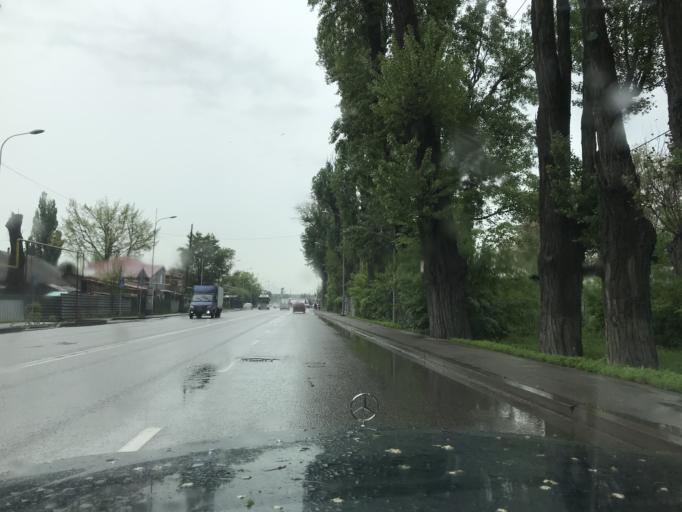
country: KZ
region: Almaty Oblysy
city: Pervomayskiy
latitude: 43.3438
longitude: 76.9673
